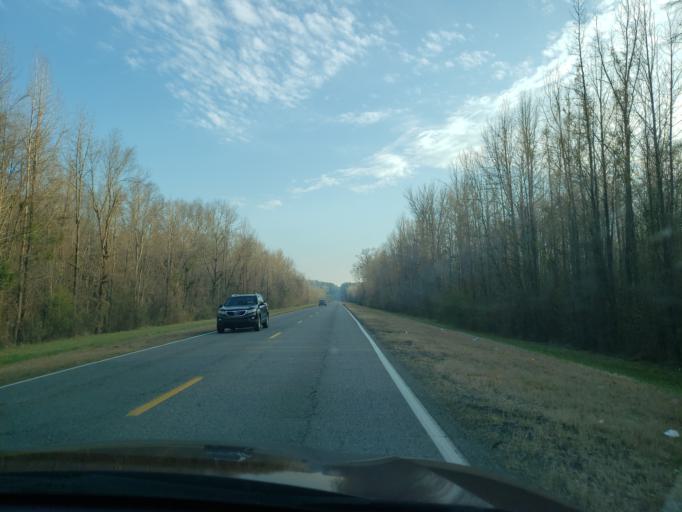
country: US
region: Alabama
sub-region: Hale County
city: Greensboro
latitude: 32.7687
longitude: -87.5855
